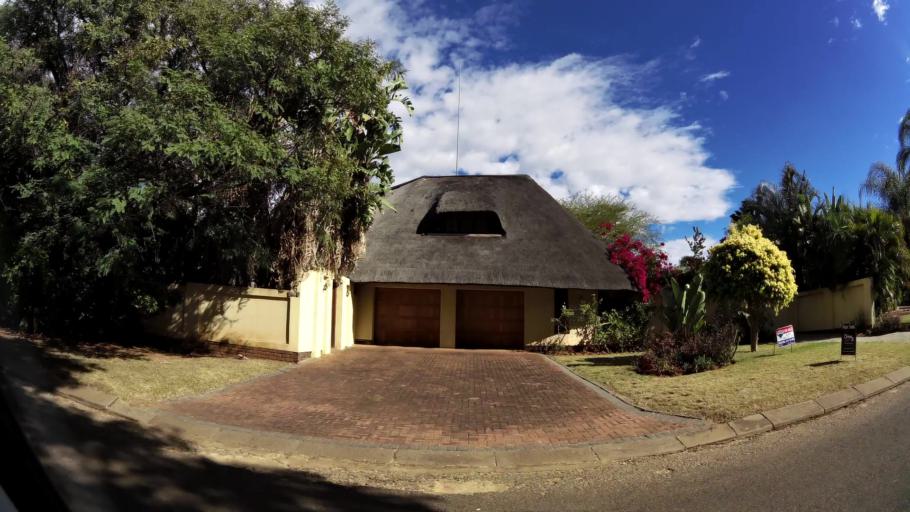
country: ZA
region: Limpopo
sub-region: Waterberg District Municipality
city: Warmbaths
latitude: -24.8732
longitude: 28.2891
